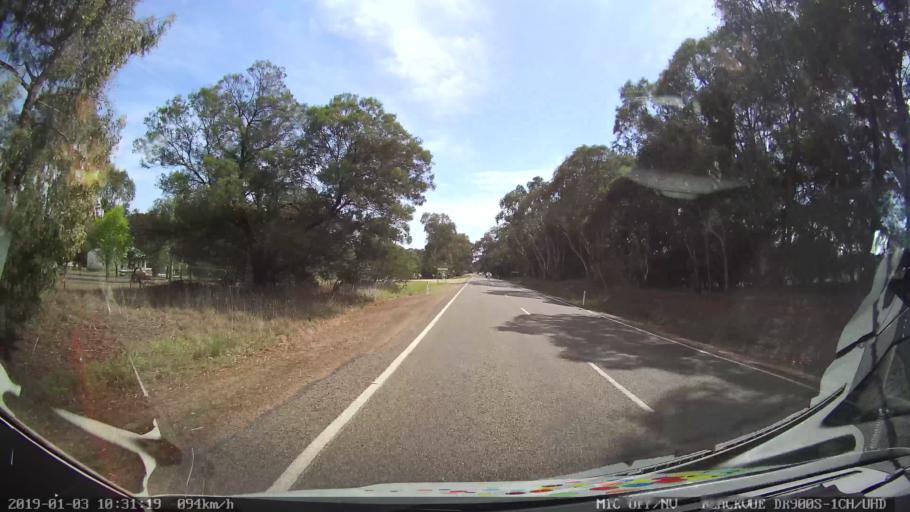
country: AU
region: New South Wales
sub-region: Young
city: Young
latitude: -34.3516
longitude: 148.2761
